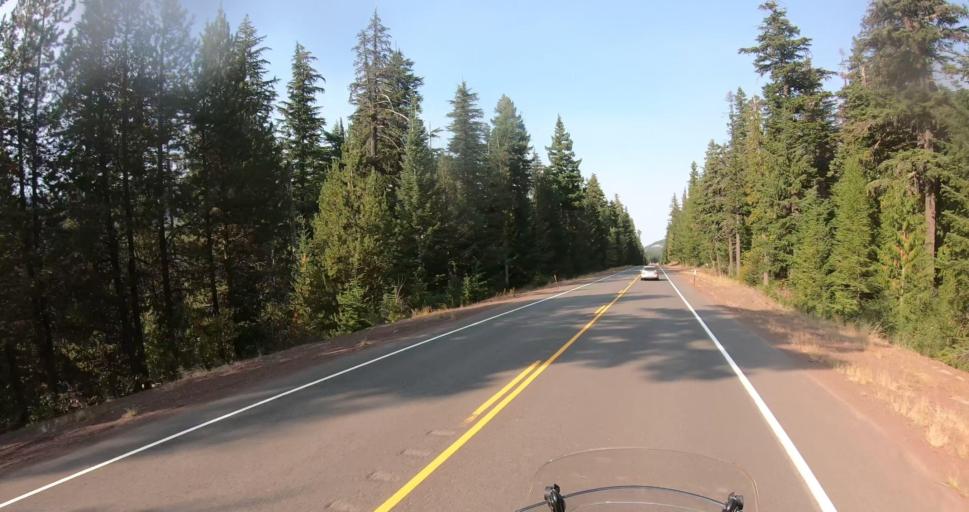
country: US
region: Oregon
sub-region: Hood River County
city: Odell
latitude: 45.3549
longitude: -121.5680
